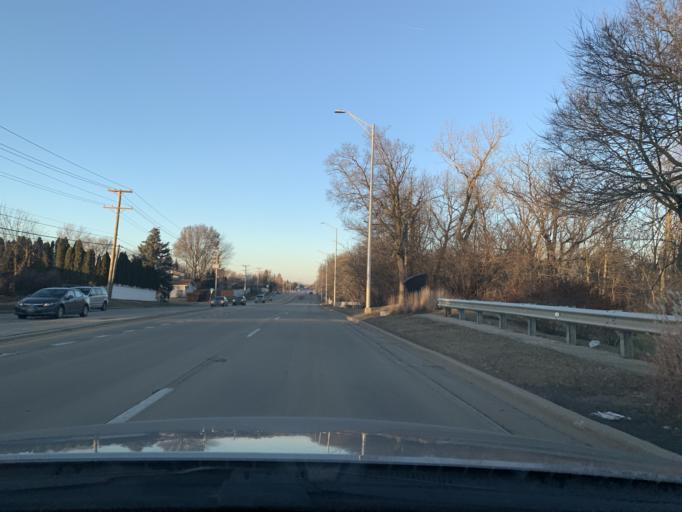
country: US
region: Illinois
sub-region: Cook County
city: Schaumburg
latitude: 42.0205
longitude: -88.0603
